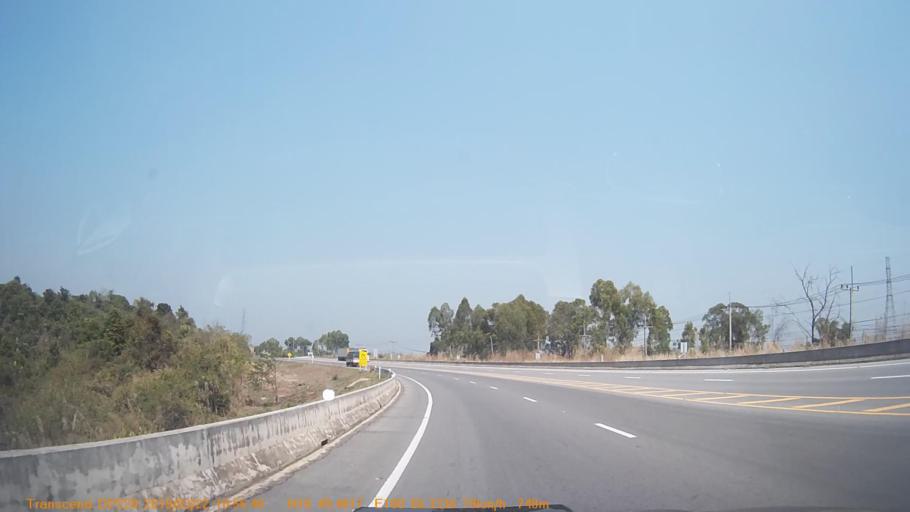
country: TH
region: Phetchabun
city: Khao Kho
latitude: 16.8243
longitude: 100.9388
